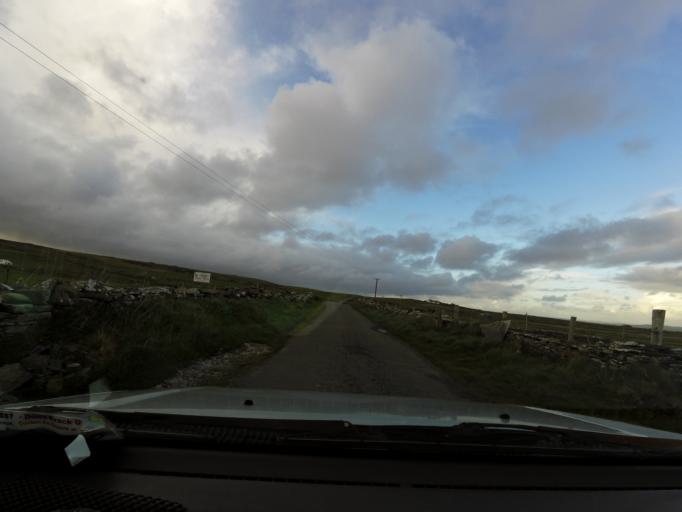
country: IE
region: Munster
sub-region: An Clar
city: Kilrush
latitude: 52.9518
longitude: -9.4414
